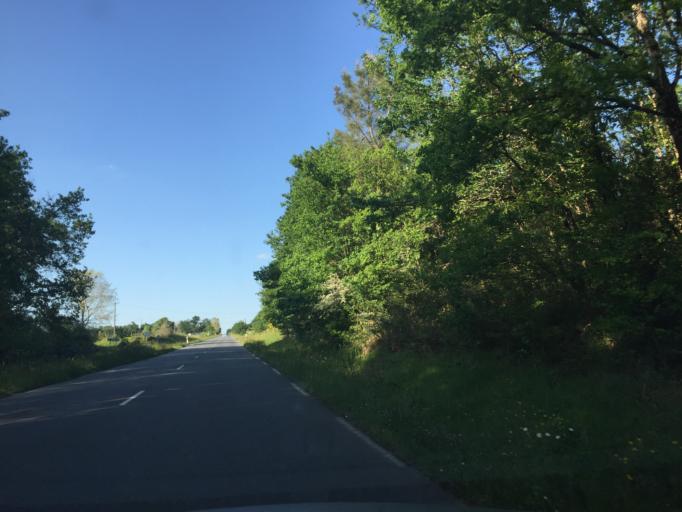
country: FR
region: Aquitaine
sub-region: Departement de la Dordogne
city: La Roche-Chalais
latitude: 45.1793
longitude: 0.0229
